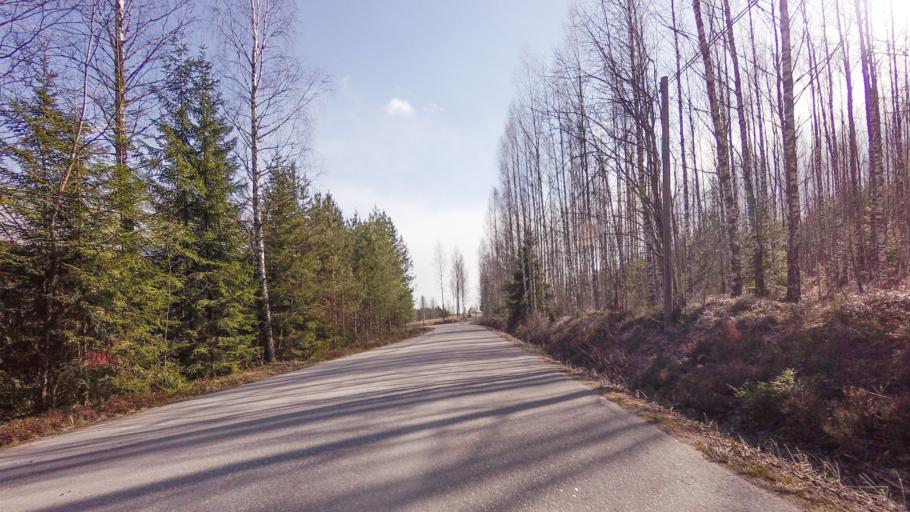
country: FI
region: Varsinais-Suomi
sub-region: Salo
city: Suomusjaervi
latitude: 60.3064
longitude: 23.6469
